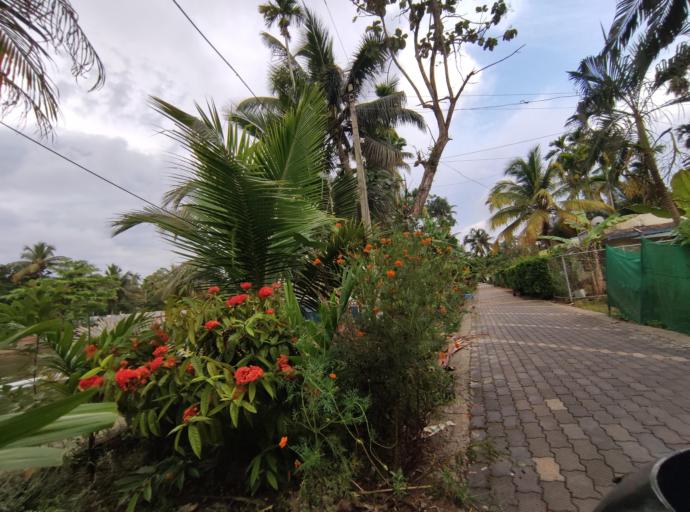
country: IN
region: Kerala
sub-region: Alappuzha
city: Shertallai
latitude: 9.6314
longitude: 76.4255
